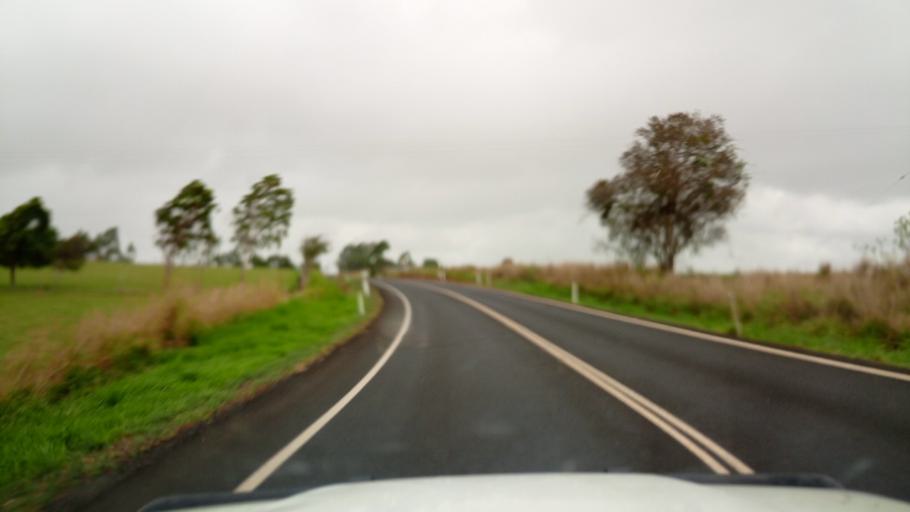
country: AU
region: Queensland
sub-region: Tablelands
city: Atherton
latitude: -17.2805
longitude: 145.6009
